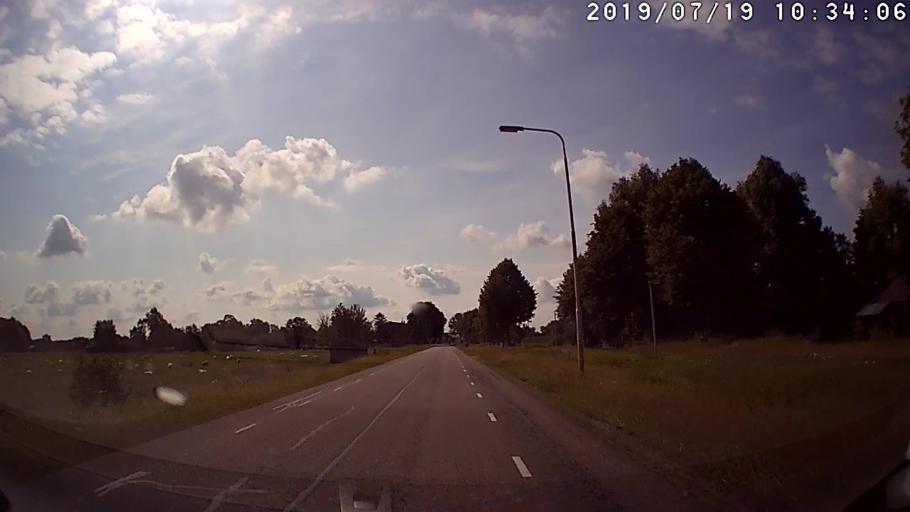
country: NL
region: Drenthe
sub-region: Gemeente Hoogeveen
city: Hoogeveen
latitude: 52.6003
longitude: 6.4188
